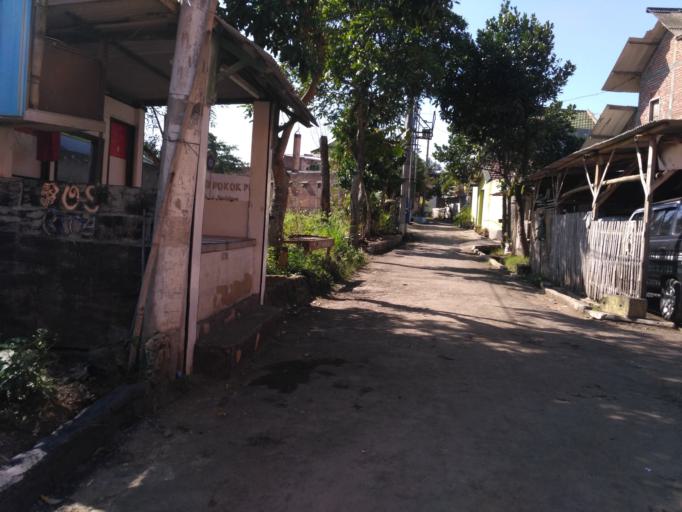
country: ID
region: East Java
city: Singosari
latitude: -7.9138
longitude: 112.6696
